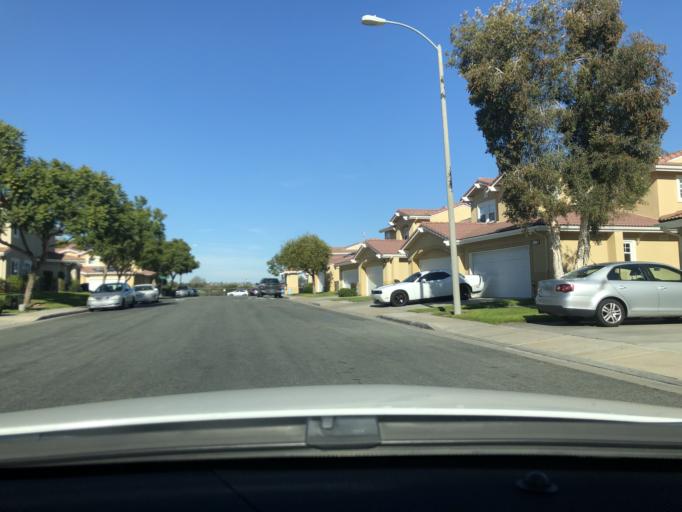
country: US
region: California
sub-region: San Diego County
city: Lemon Grove
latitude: 32.7391
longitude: -117.0624
